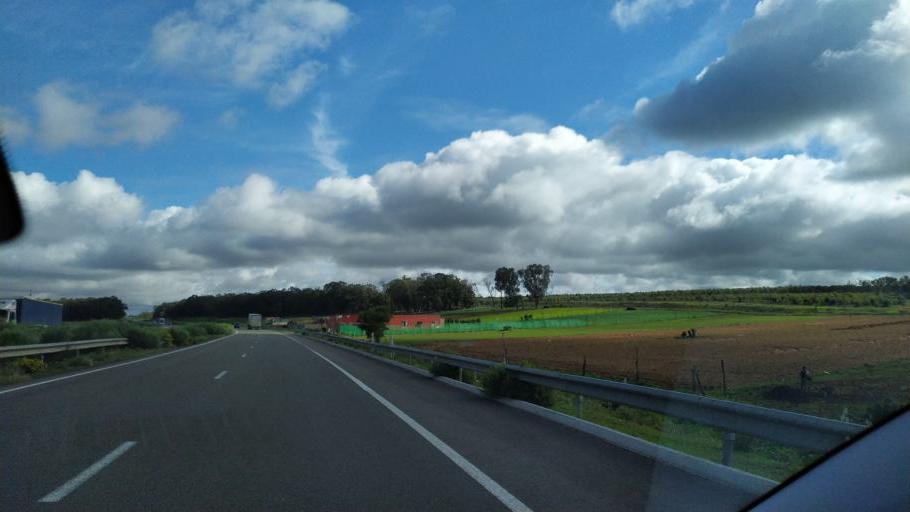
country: MA
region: Gharb-Chrarda-Beni Hssen
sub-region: Kenitra Province
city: Lalla Mimouna
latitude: 34.8027
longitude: -6.2635
